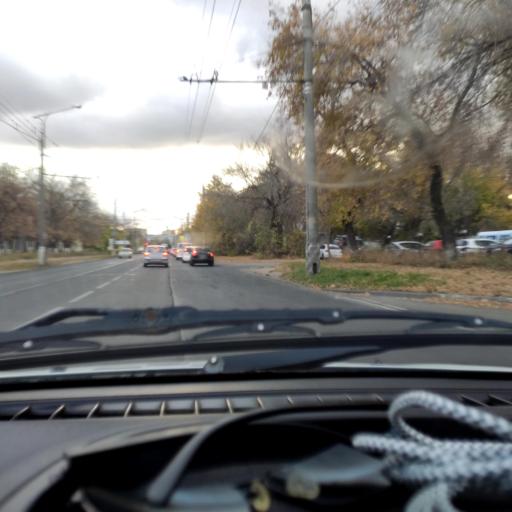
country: RU
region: Samara
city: Tol'yatti
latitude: 53.5188
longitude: 49.4315
